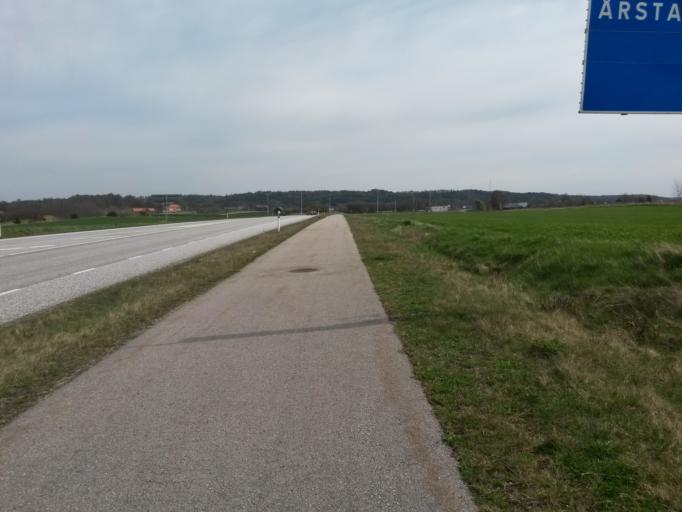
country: SE
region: Halland
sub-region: Falkenbergs Kommun
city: Falkenberg
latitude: 56.8835
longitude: 12.6129
